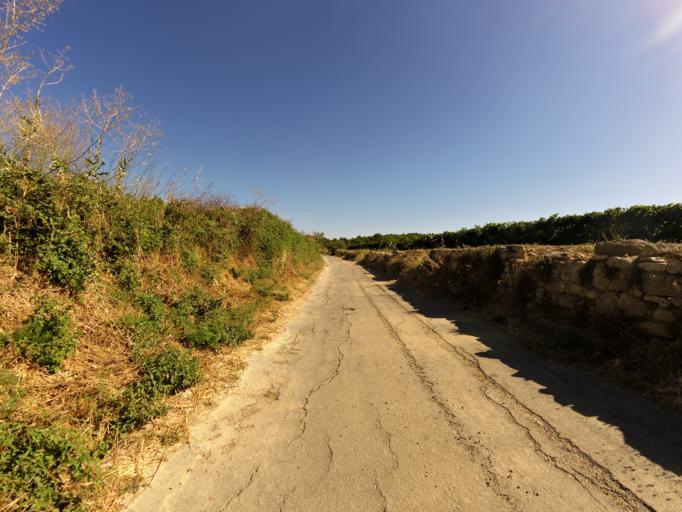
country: FR
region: Languedoc-Roussillon
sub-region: Departement du Gard
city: Aigues-Vives
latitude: 43.7519
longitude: 4.1857
